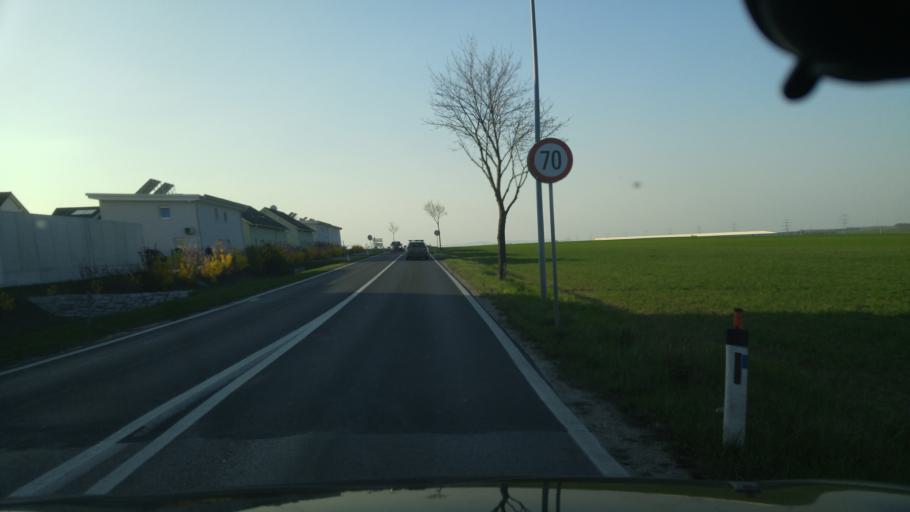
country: AT
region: Lower Austria
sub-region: Politischer Bezirk Wien-Umgebung
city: Gramatneusiedl
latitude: 48.0322
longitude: 16.4857
